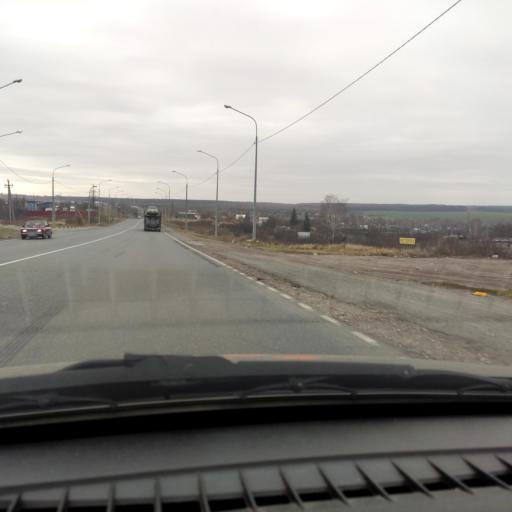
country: RU
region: Samara
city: Zhigulevsk
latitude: 53.3723
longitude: 49.4568
